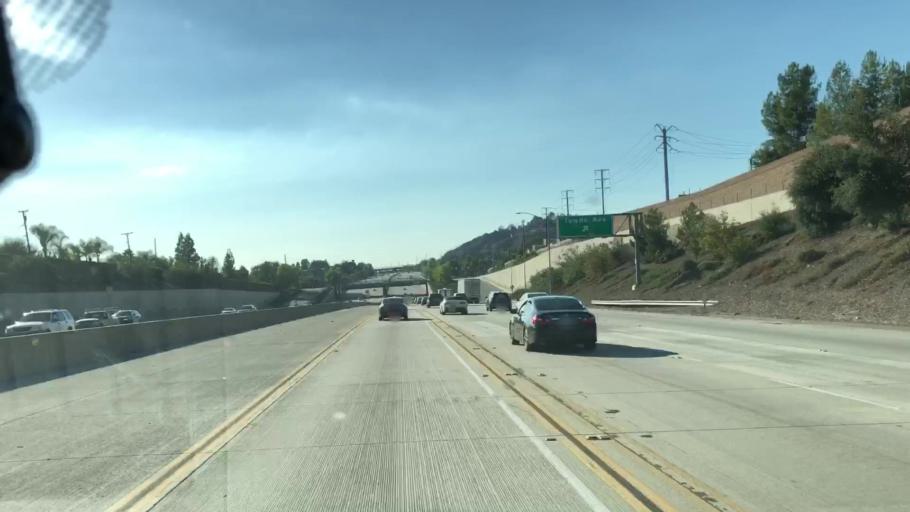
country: US
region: California
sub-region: Los Angeles County
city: Claremont
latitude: 34.1210
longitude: -117.7303
